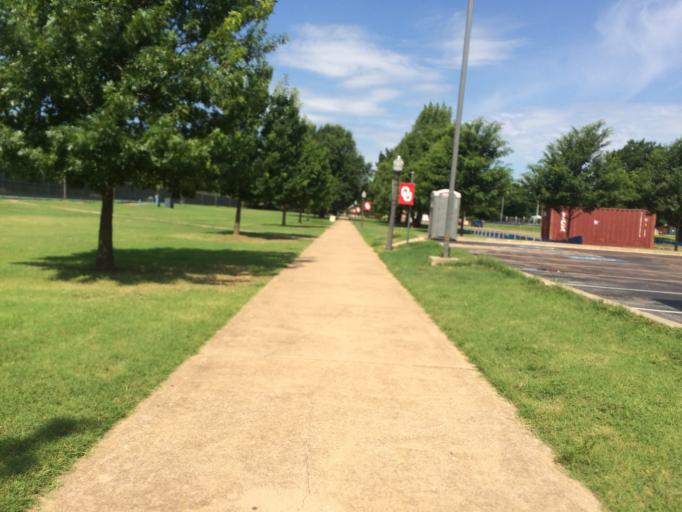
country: US
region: Oklahoma
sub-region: Cleveland County
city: Norman
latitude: 35.1964
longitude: -97.4418
